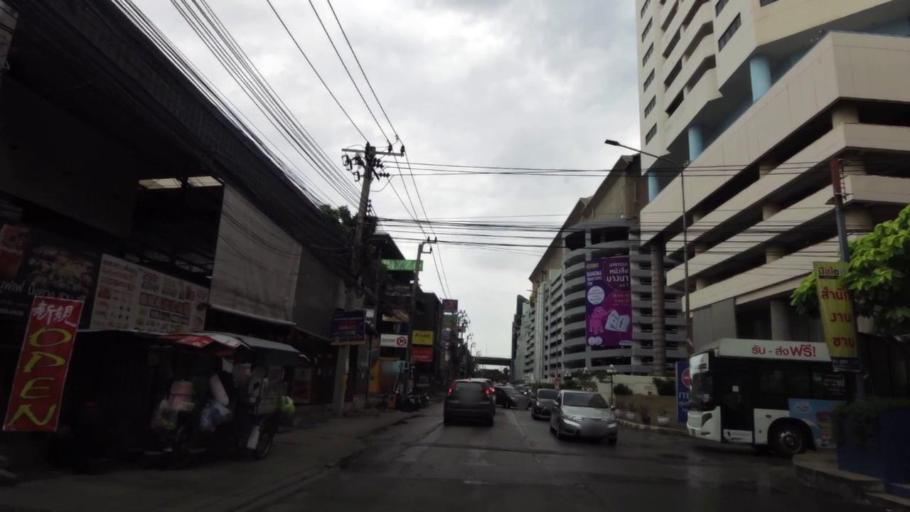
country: TH
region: Bangkok
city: Bang Na
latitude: 13.6712
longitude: 100.6359
